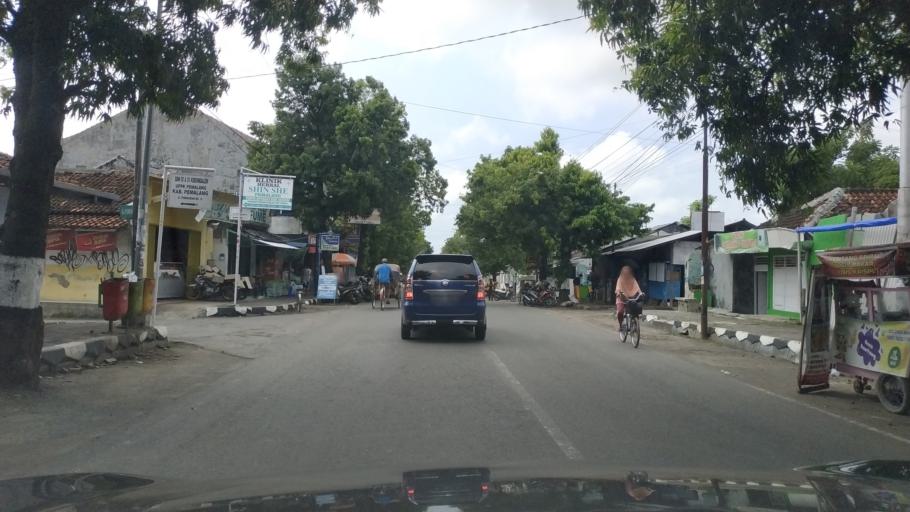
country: ID
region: Central Java
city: Pemalang
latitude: -6.8937
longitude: 109.3828
